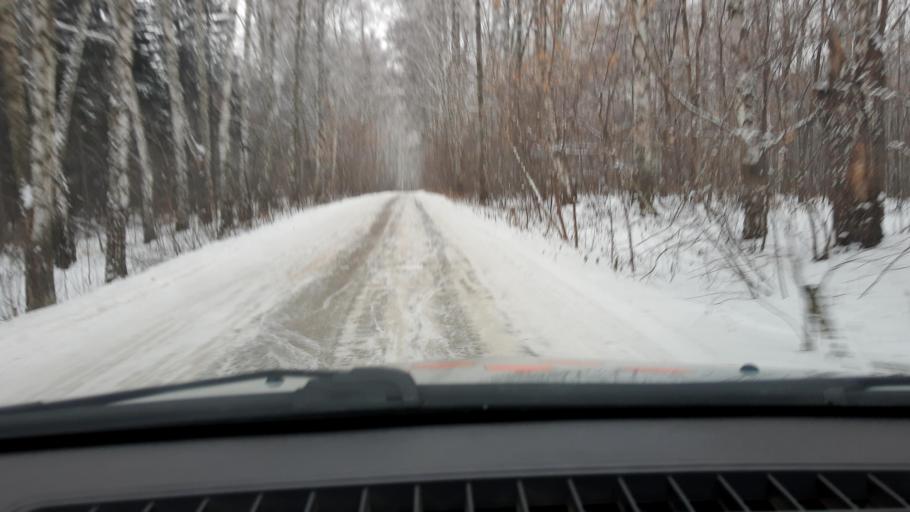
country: RU
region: Bashkortostan
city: Iglino
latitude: 54.8264
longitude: 56.1938
